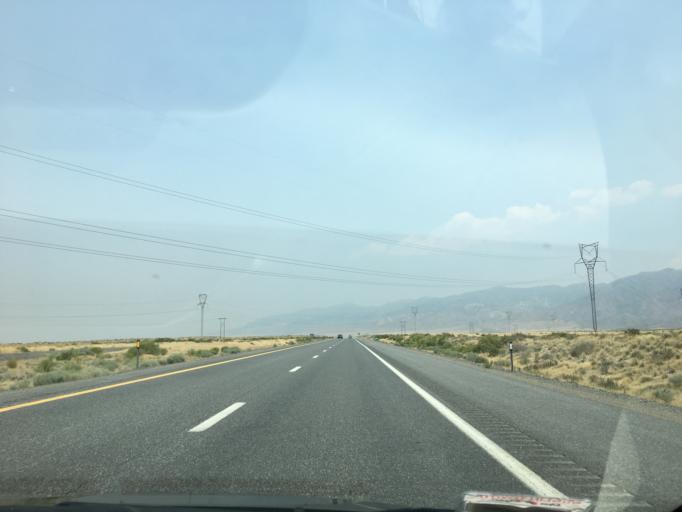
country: US
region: Nevada
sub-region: Pershing County
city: Lovelock
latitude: 40.3108
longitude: -118.3380
